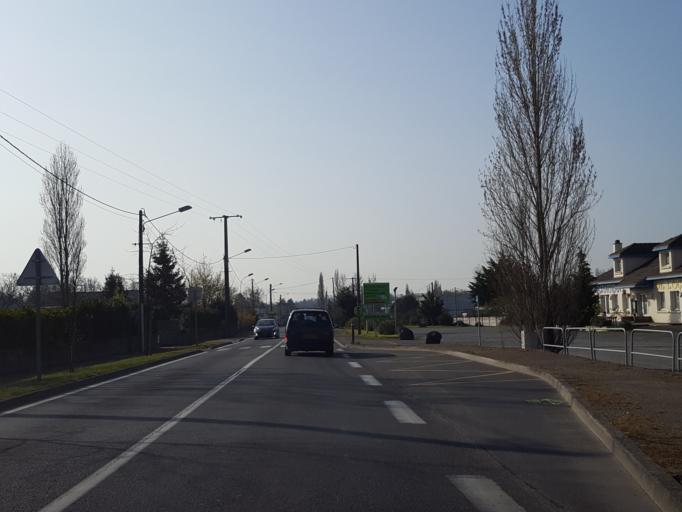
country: FR
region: Pays de la Loire
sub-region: Departement de la Loire-Atlantique
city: Geneston
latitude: 47.0660
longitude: -1.5179
